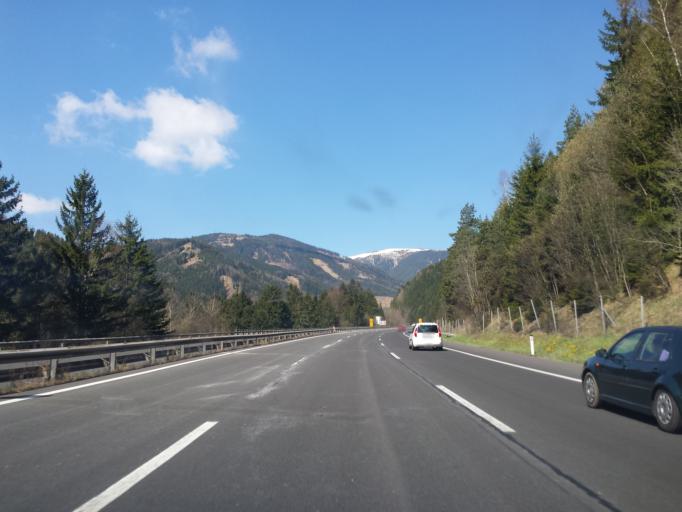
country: AT
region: Styria
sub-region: Politischer Bezirk Graz-Umgebung
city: Ubelbach
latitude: 47.2445
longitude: 15.1829
